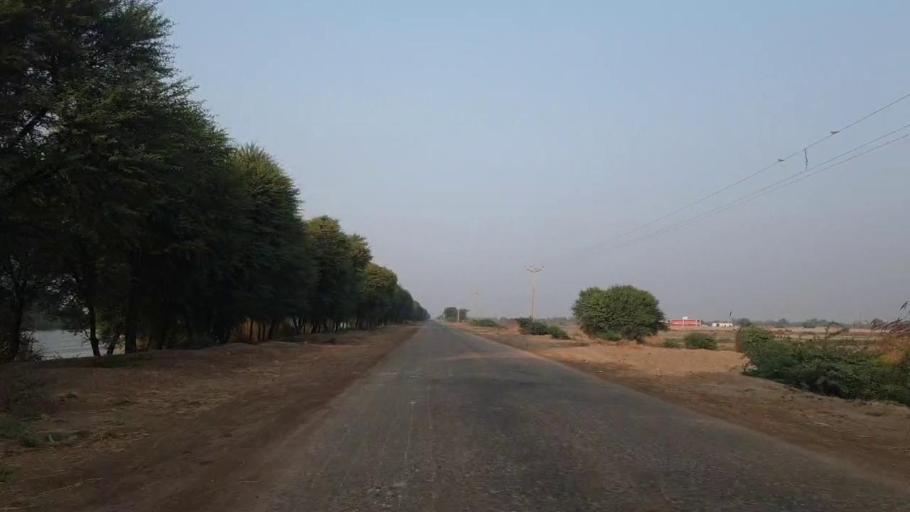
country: PK
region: Sindh
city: Tando Muhammad Khan
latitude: 25.1206
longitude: 68.4288
